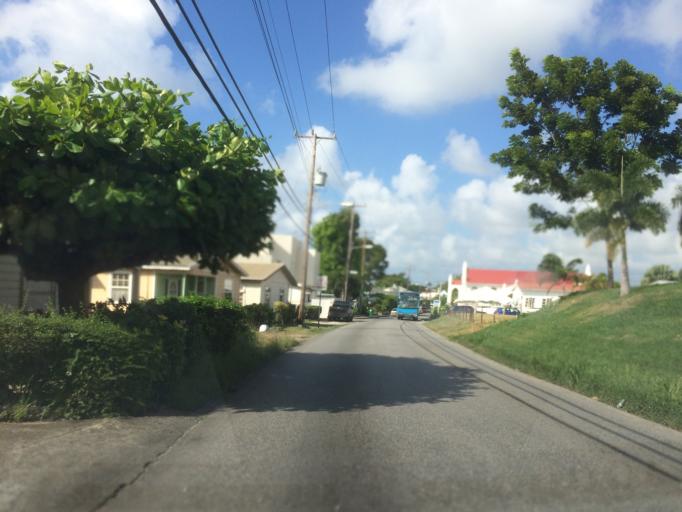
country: BB
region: Saint James
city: Holetown
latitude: 13.2040
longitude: -59.6397
